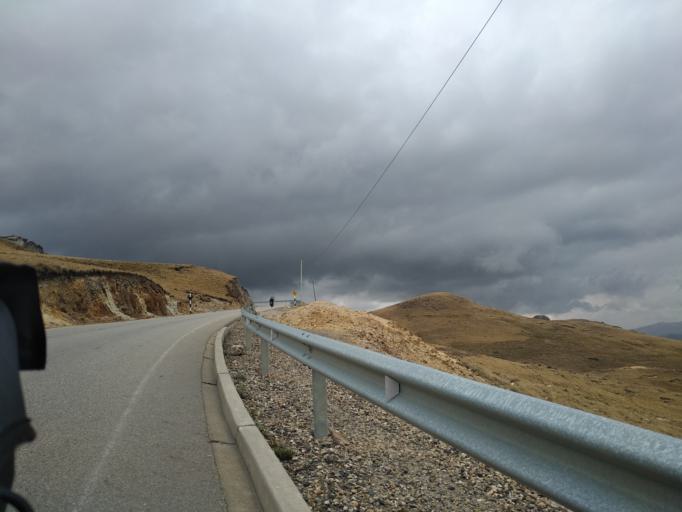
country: PE
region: La Libertad
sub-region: Provincia de Santiago de Chuco
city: Quiruvilca
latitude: -7.9889
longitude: -78.2825
